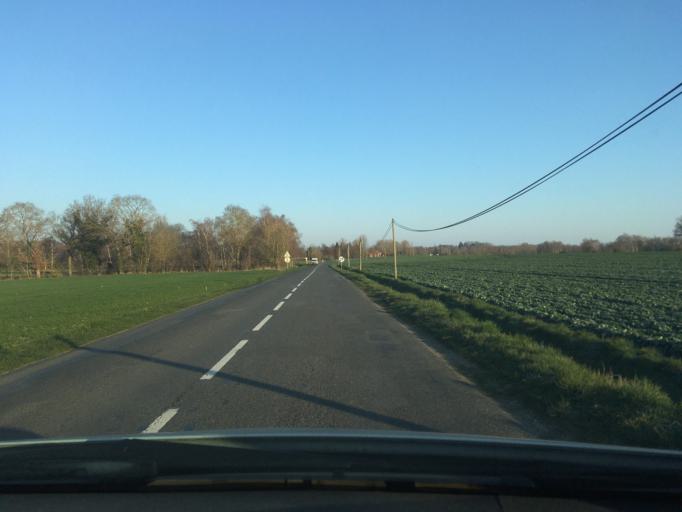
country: FR
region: Rhone-Alpes
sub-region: Departement de l'Ain
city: Saint-Andre-de-Corcy
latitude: 45.9609
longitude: 4.9409
